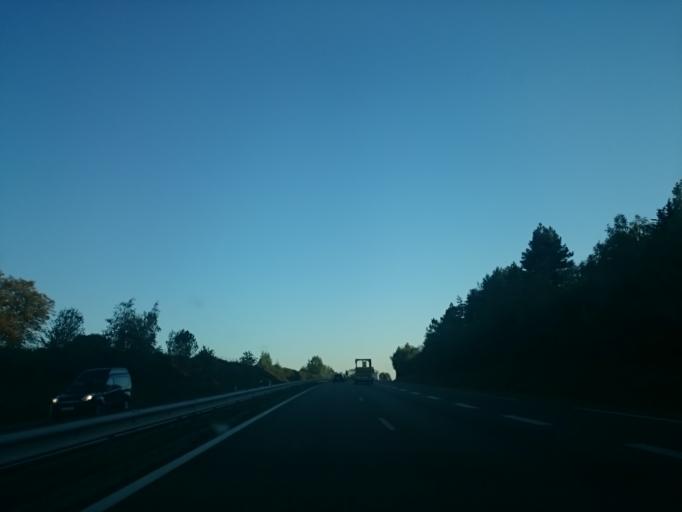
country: FR
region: Brittany
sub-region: Departement d'Ille-et-Vilaine
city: Bain-de-Bretagne
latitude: 47.8287
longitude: -1.6897
